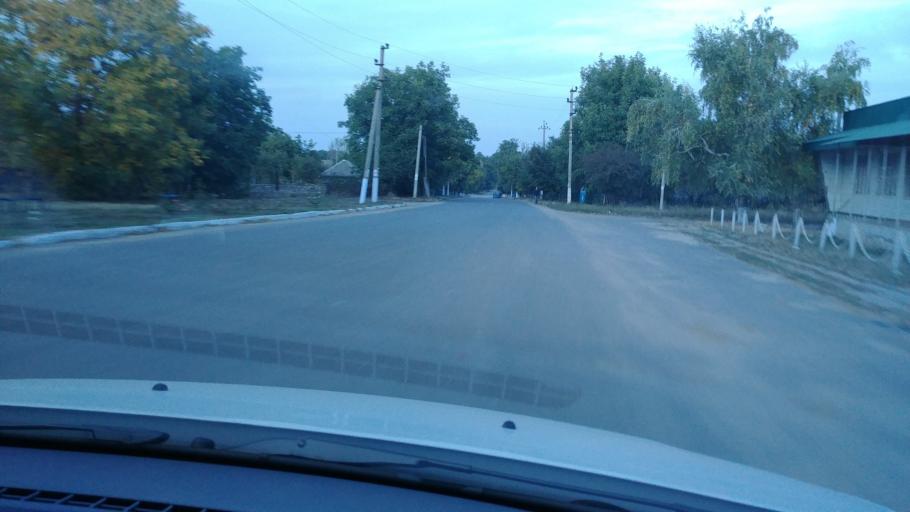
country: MD
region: Rezina
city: Saharna
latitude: 47.6741
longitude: 28.9571
